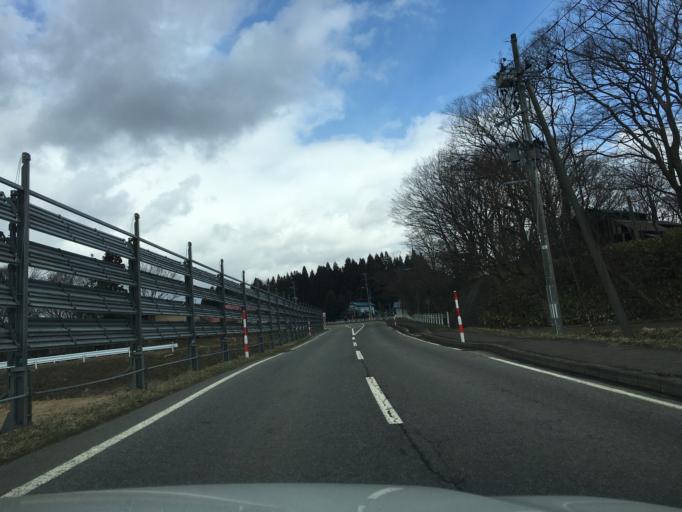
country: JP
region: Akita
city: Takanosu
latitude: 40.1535
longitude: 140.3353
